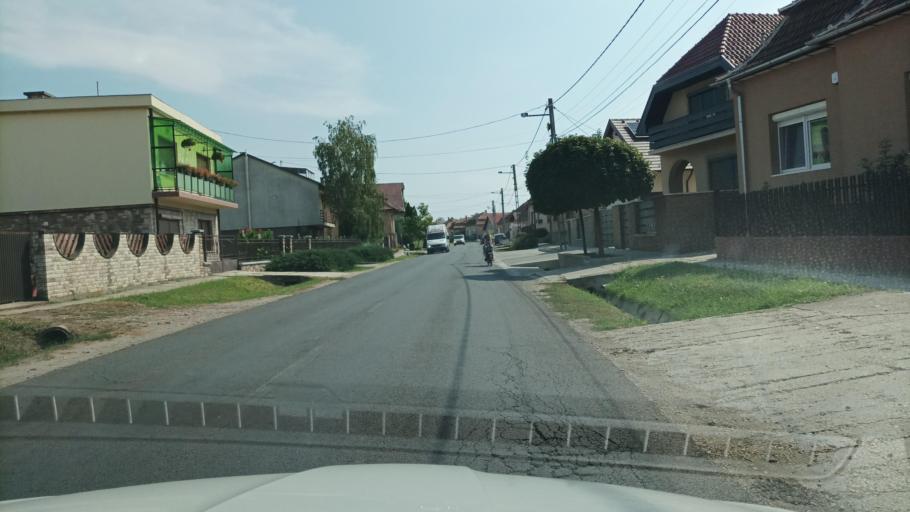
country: HU
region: Pest
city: Galgaheviz
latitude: 47.6210
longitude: 19.5597
